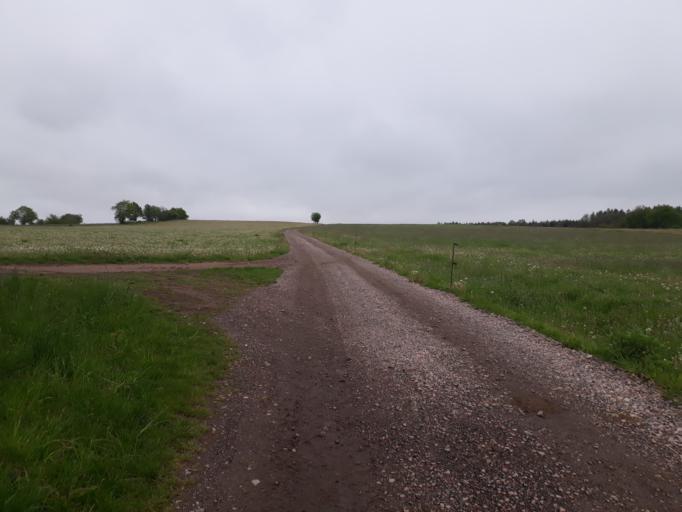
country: DE
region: Saxony
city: Reinhardtsgrimma
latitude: 50.8889
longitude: 13.7533
